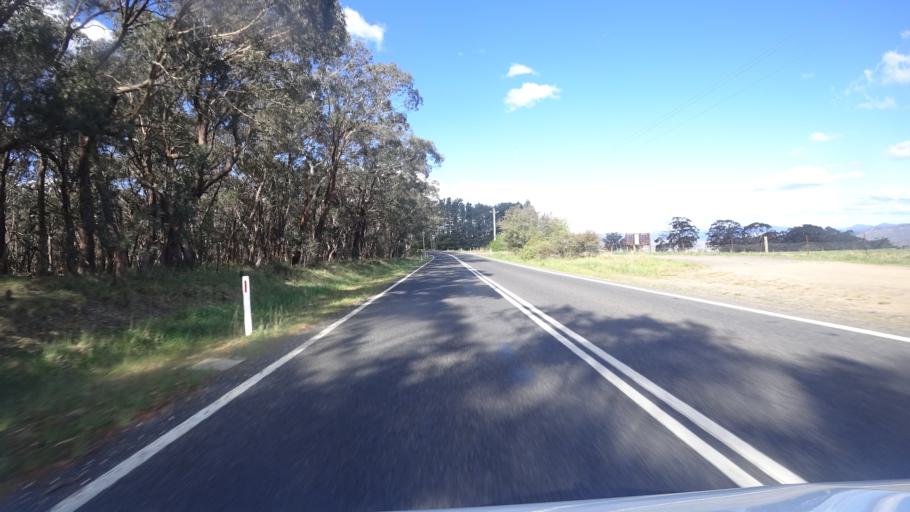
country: AU
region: New South Wales
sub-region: Lithgow
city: Bowenfels
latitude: -33.6369
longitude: 150.0758
